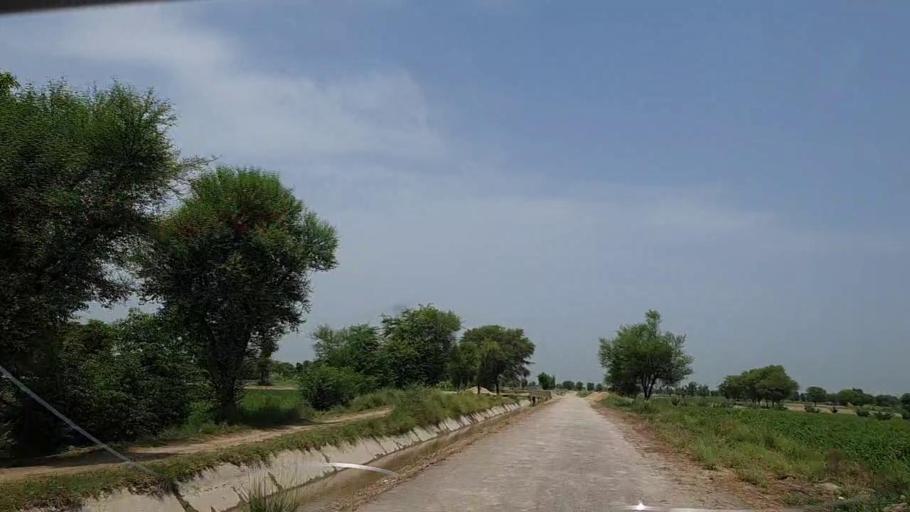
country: PK
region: Sindh
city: Tharu Shah
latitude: 26.9363
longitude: 68.0682
